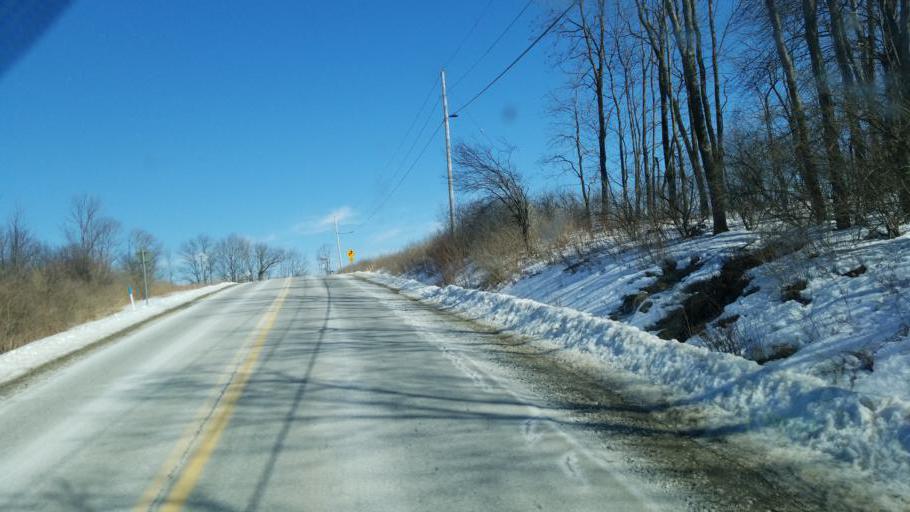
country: US
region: New York
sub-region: Allegany County
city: Alfred
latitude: 42.2676
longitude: -77.7353
